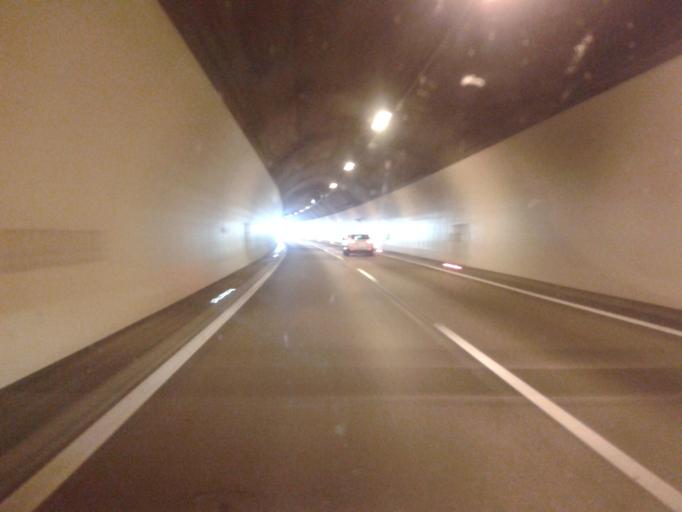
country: AT
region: Carinthia
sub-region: Politischer Bezirk Wolfsberg
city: Wolfsberg
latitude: 46.9022
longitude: 14.8219
